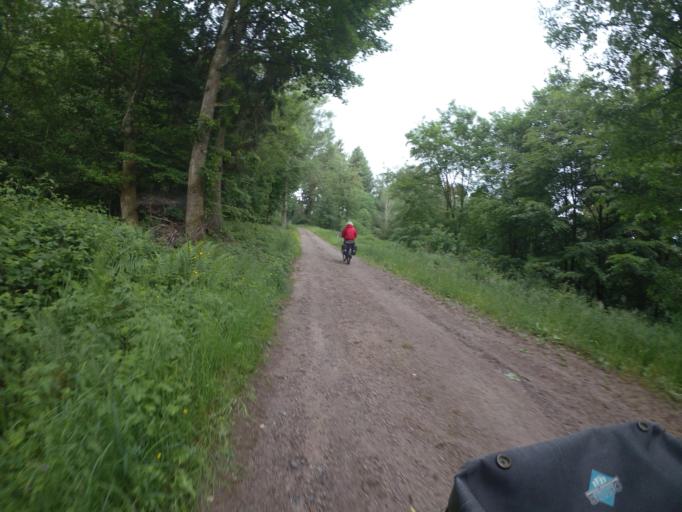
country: DE
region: Rheinland-Pfalz
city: Obersimten
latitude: 49.1701
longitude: 7.5992
